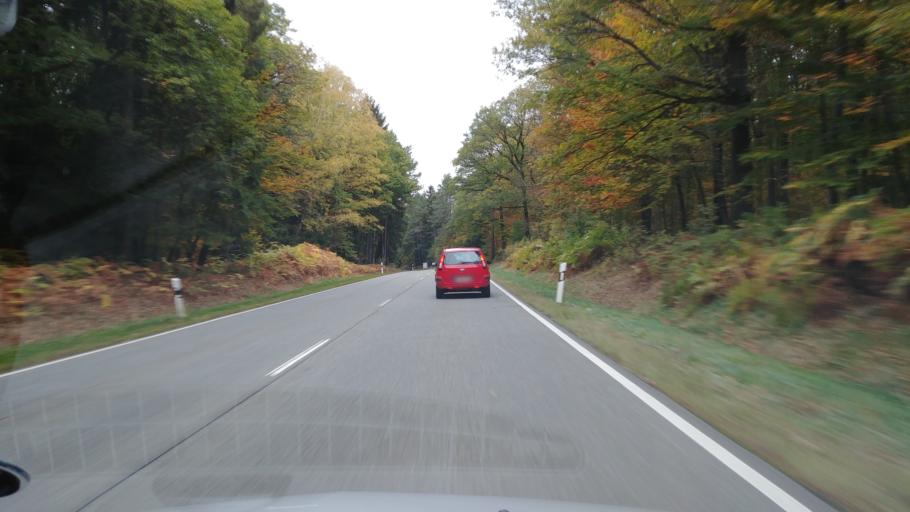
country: DE
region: Rheinland-Pfalz
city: Hilscheid
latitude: 49.7363
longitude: 7.0216
